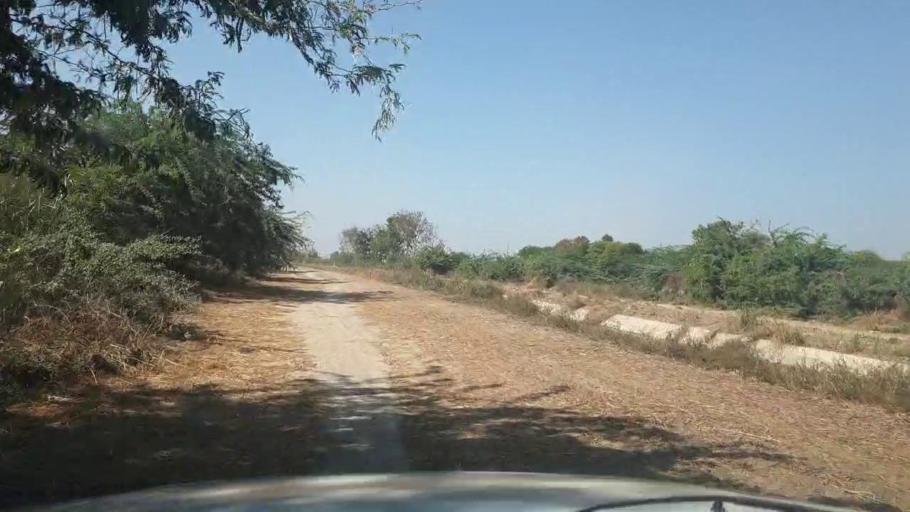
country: PK
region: Sindh
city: Chuhar Jamali
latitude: 24.4257
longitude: 67.7973
